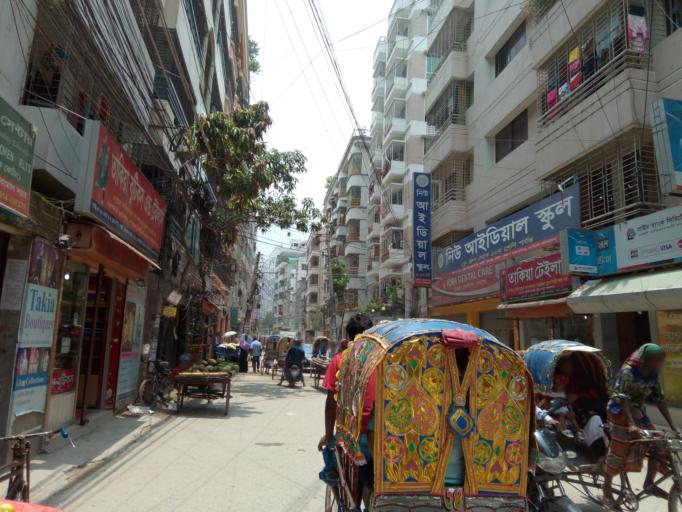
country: BD
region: Dhaka
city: Paltan
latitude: 23.7618
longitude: 90.4321
